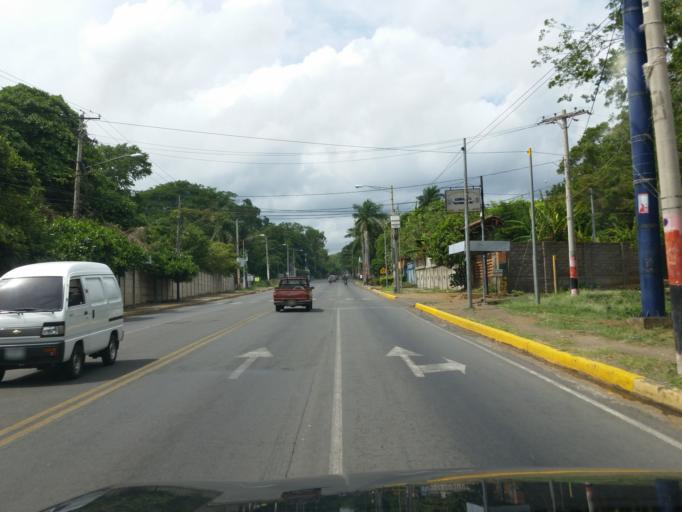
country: NI
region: Managua
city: Ciudad Sandino
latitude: 12.0872
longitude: -86.3239
